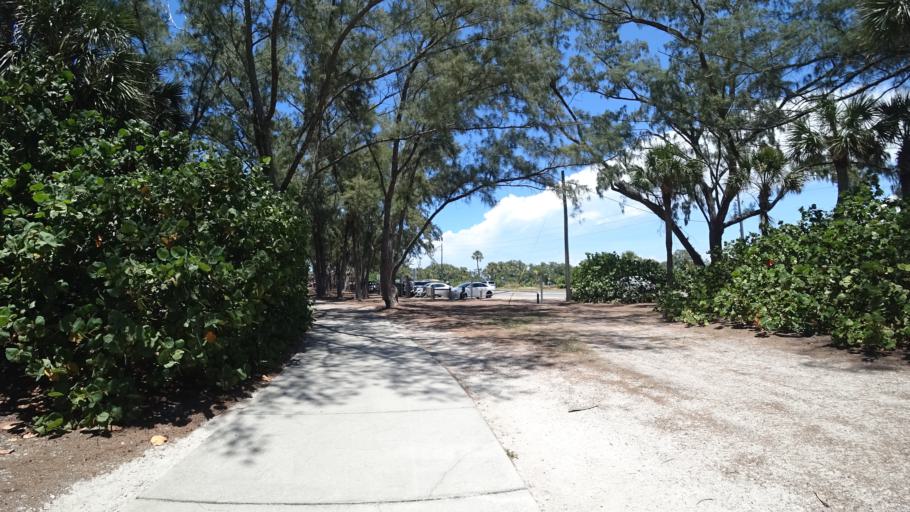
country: US
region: Florida
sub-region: Manatee County
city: Bradenton Beach
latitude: 27.4553
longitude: -82.6945
